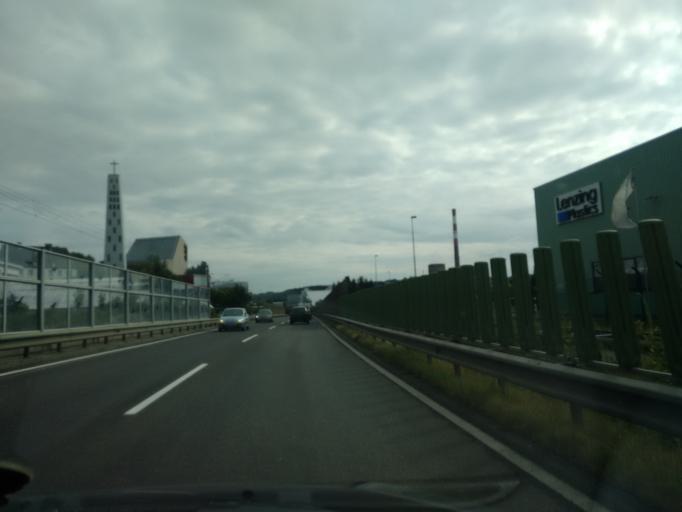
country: AT
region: Upper Austria
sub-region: Politischer Bezirk Vocklabruck
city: Lenzing
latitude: 47.9734
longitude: 13.6096
